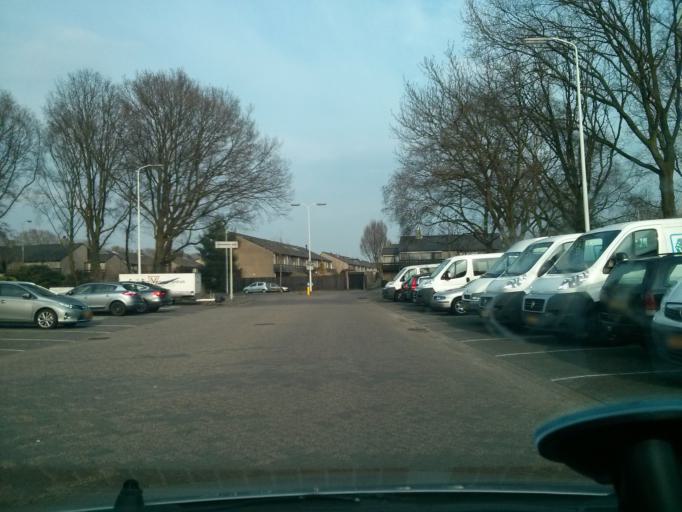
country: NL
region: North Brabant
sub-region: Gemeente Son en Breugel
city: Son
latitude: 51.4825
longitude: 5.4604
